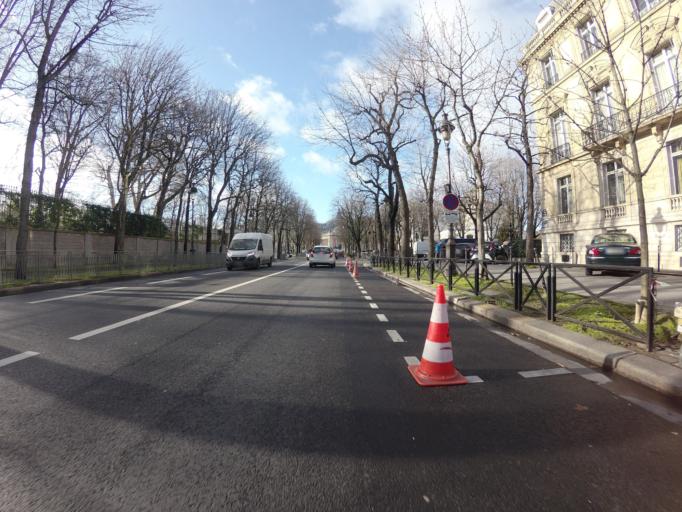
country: FR
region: Ile-de-France
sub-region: Departement des Hauts-de-Seine
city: Clichy
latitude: 48.8692
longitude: 2.3149
